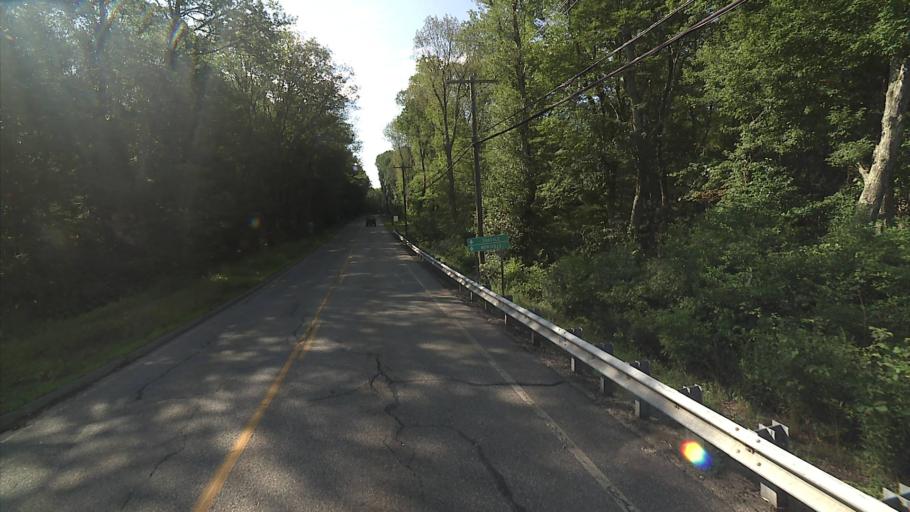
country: US
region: Connecticut
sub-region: New London County
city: Montville Center
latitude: 41.5013
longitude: -72.2006
